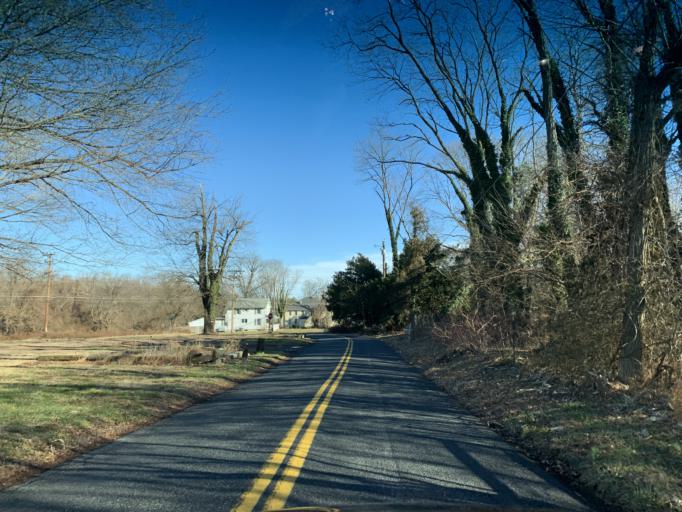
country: US
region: Maryland
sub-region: Harford County
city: Riverside
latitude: 39.5423
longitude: -76.2359
